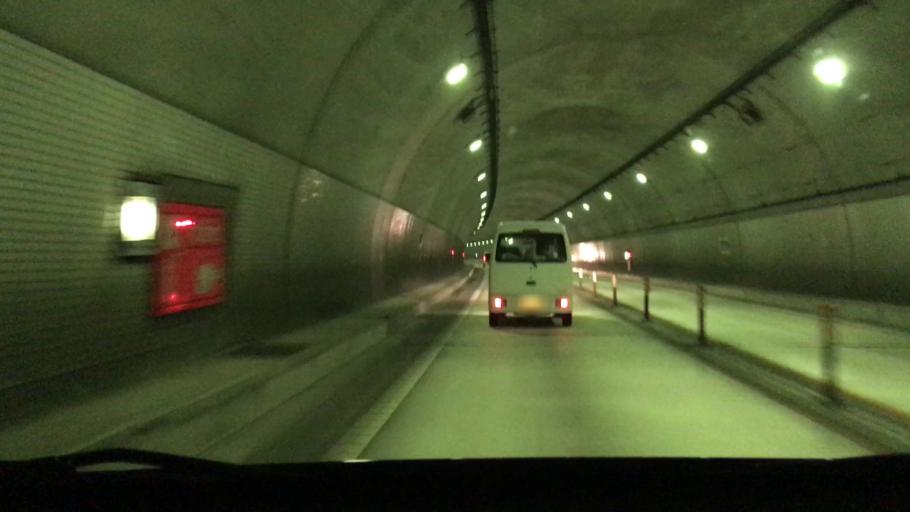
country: JP
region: Nagasaki
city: Sasebo
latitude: 33.0937
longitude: 129.7788
